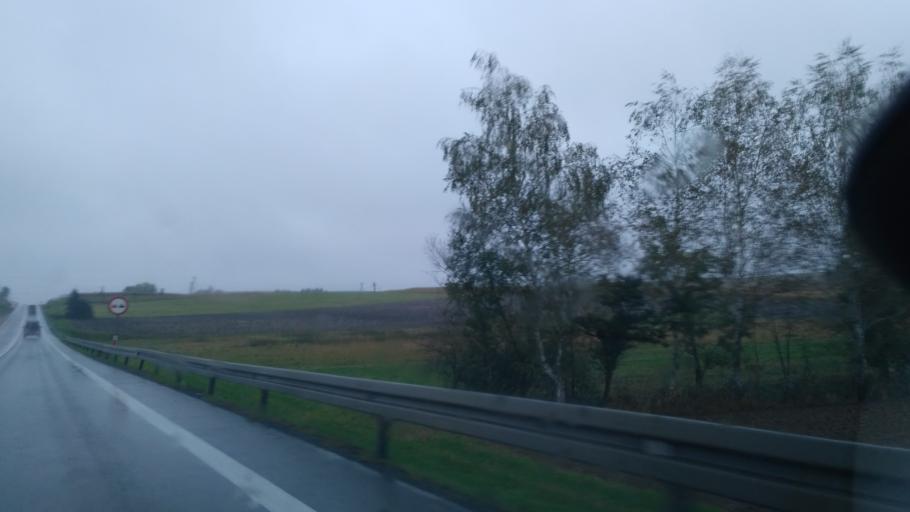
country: PL
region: Subcarpathian Voivodeship
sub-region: Powiat krosnienski
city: Miejsce Piastowe
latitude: 49.6277
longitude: 21.7746
